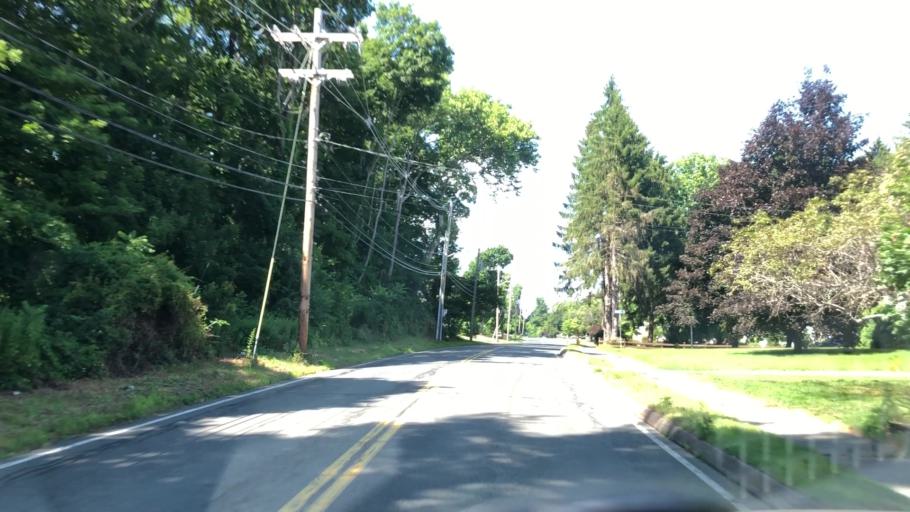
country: US
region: Massachusetts
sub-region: Hampden County
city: Holyoke
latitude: 42.1888
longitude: -72.6500
